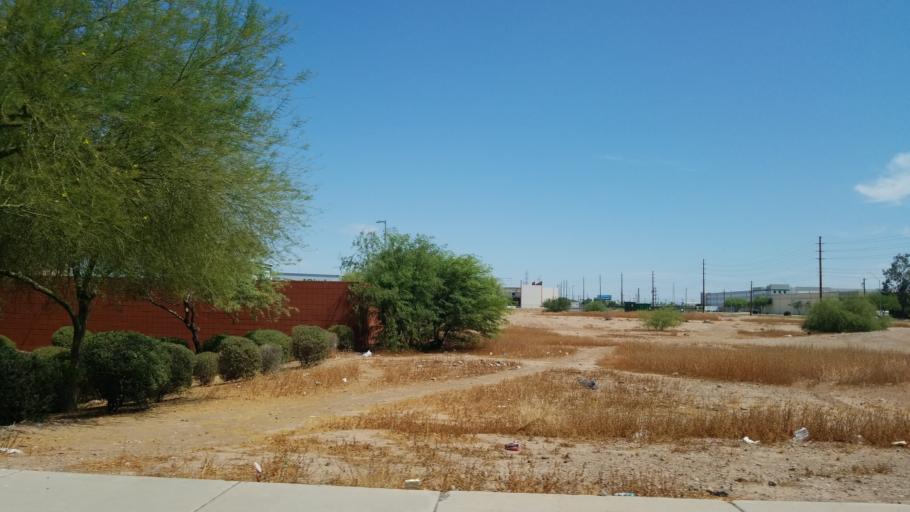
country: US
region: Arizona
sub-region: Maricopa County
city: Laveen
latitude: 33.4314
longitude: -112.1528
